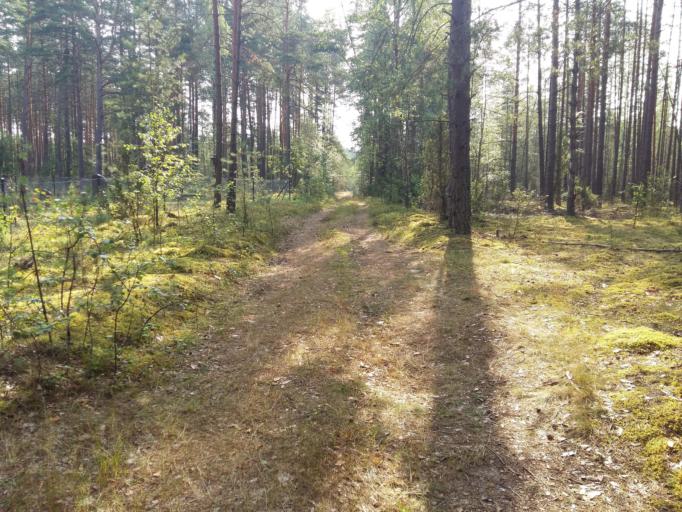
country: LT
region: Alytaus apskritis
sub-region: Alytus
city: Alytus
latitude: 54.1878
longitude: 24.1195
